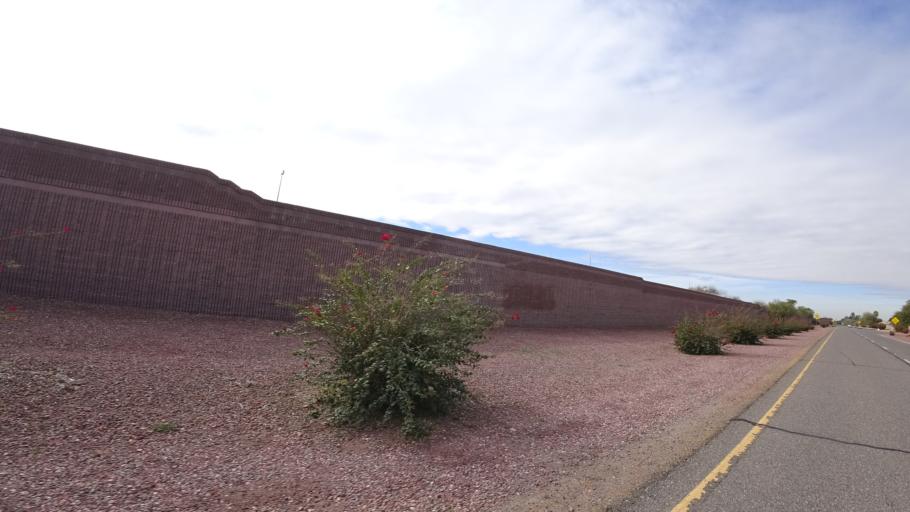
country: US
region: Arizona
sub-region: Maricopa County
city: Peoria
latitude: 33.6690
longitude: -112.1745
